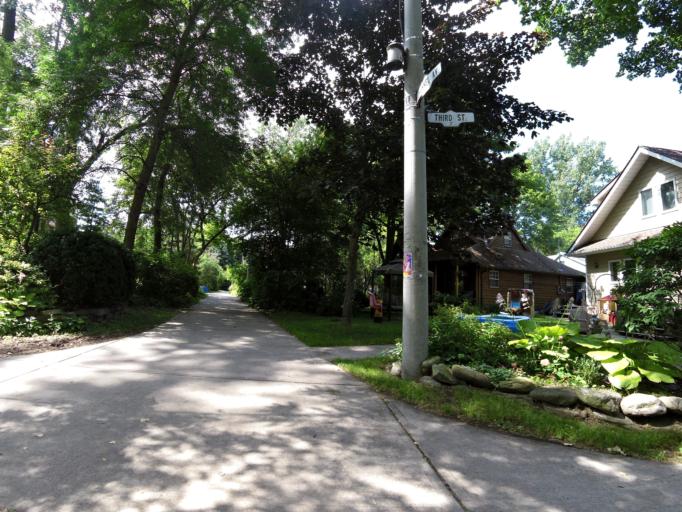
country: CA
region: Ontario
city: Toronto
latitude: 43.6327
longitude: -79.3552
